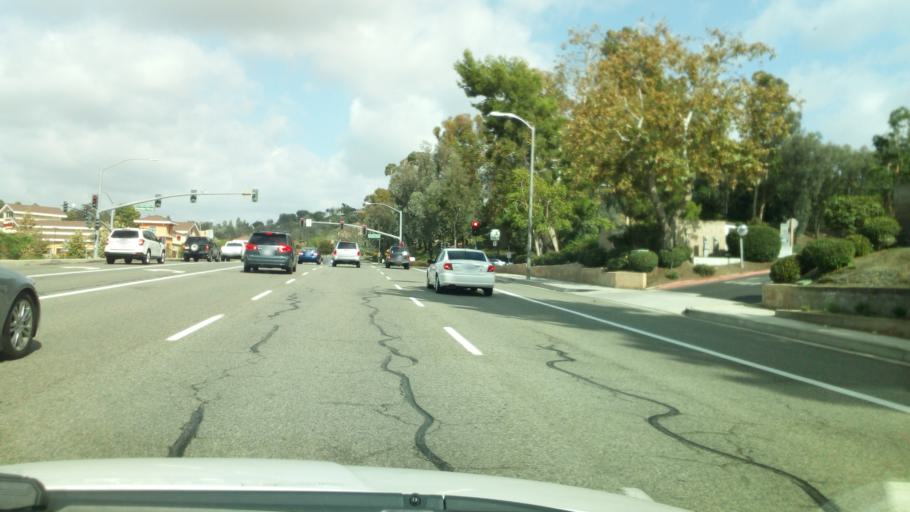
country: US
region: California
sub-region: Orange County
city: Aliso Viejo
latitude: 33.5757
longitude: -117.7031
